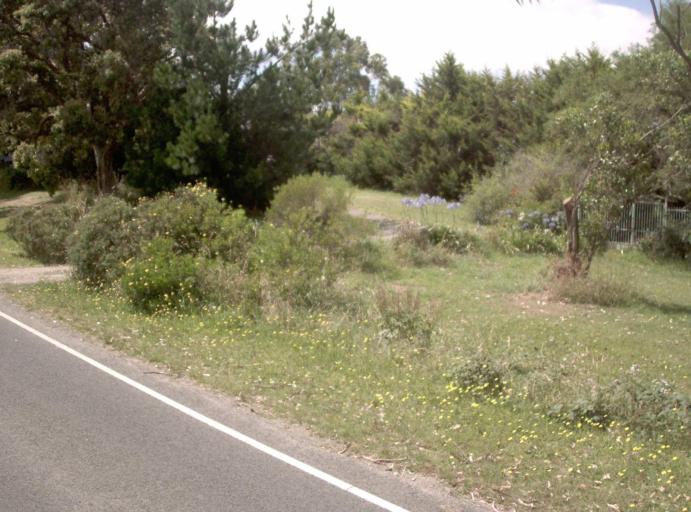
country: AU
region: Victoria
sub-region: Cardinia
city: Bunyip
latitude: -38.3434
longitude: 145.7581
